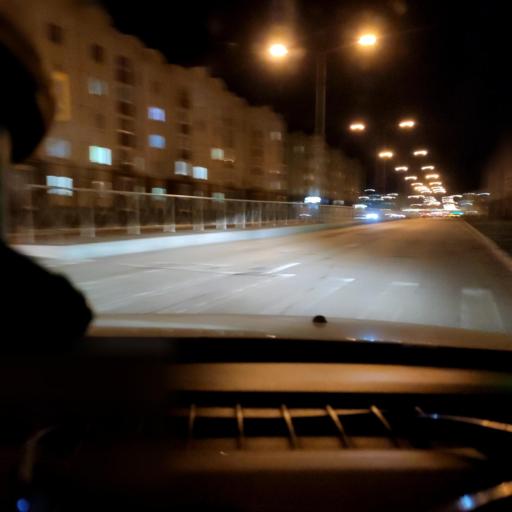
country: RU
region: Samara
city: Samara
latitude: 53.1171
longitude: 50.1578
